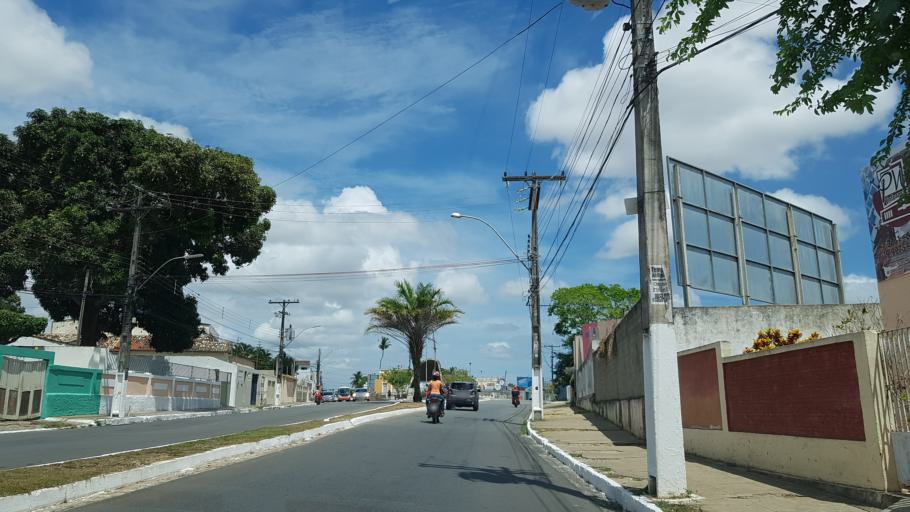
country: BR
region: Alagoas
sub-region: Penedo
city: Penedo
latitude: -10.2831
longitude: -36.5684
